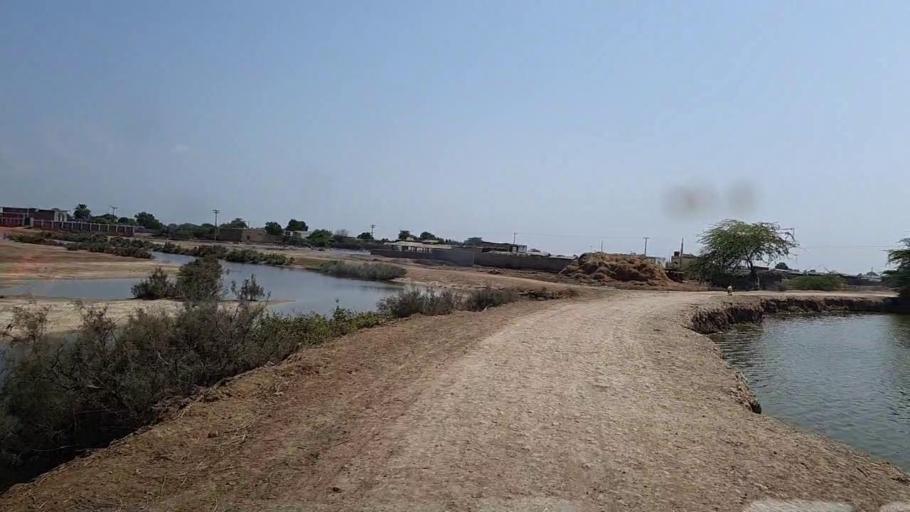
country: PK
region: Sindh
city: Kario
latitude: 24.6372
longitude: 68.4903
